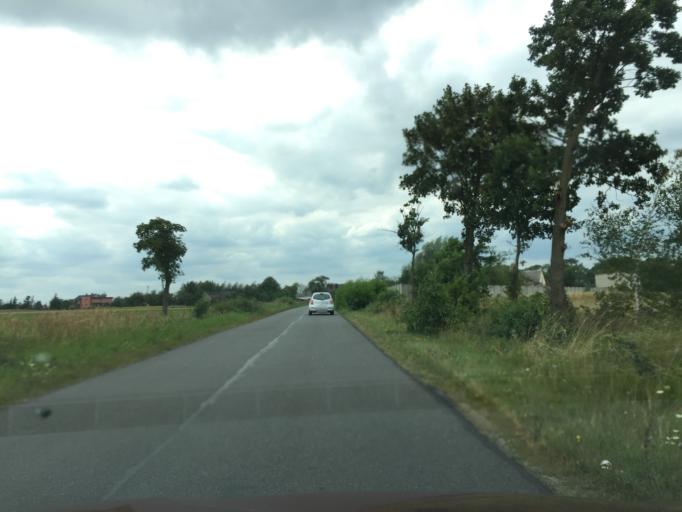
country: PL
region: Greater Poland Voivodeship
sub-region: Powiat kaliski
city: Stawiszyn
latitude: 51.9484
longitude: 18.1680
